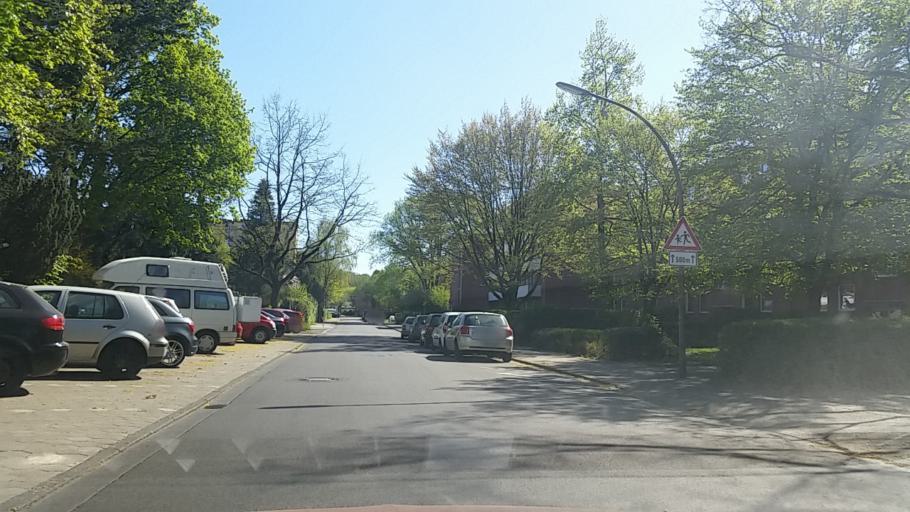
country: DE
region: Schleswig-Holstein
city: Halstenbek
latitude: 53.5823
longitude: 9.8300
